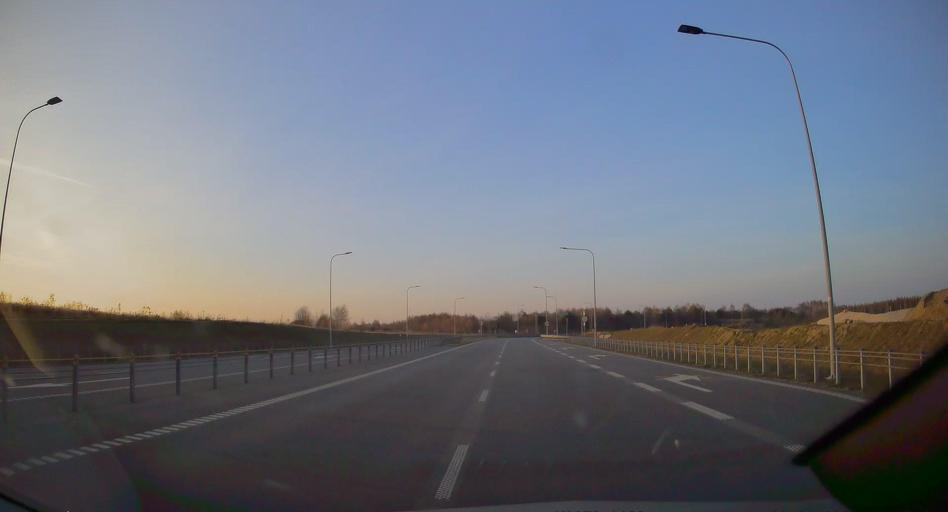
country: PL
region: Silesian Voivodeship
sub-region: Powiat klobucki
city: Kamyk
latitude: 50.8493
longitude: 19.0377
